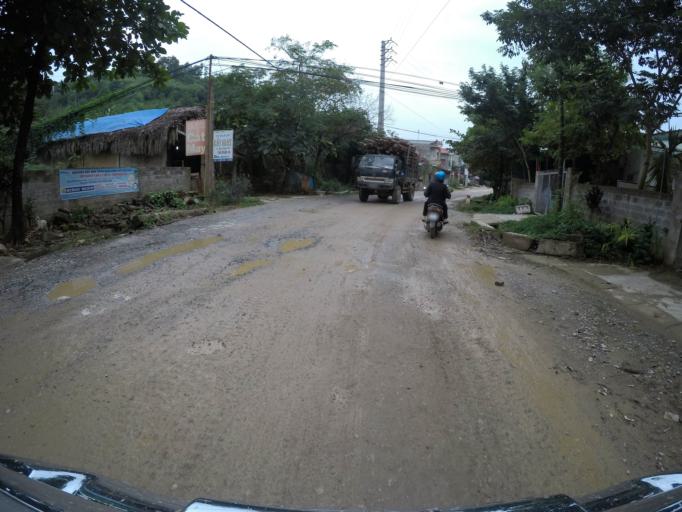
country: VN
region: Yen Bai
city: Co Phuc
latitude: 21.8709
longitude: 104.6529
